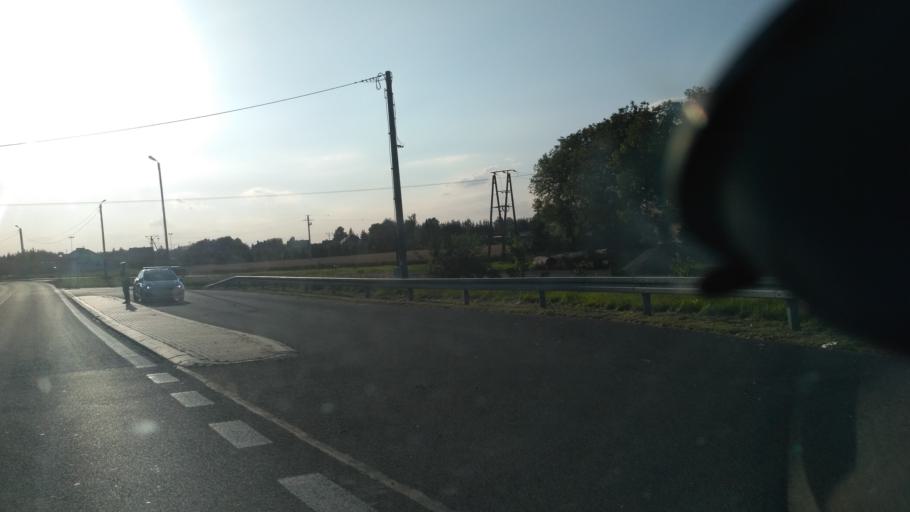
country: PL
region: Subcarpathian Voivodeship
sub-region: Powiat lezajski
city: Stare Miasto
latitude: 50.2917
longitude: 22.4382
